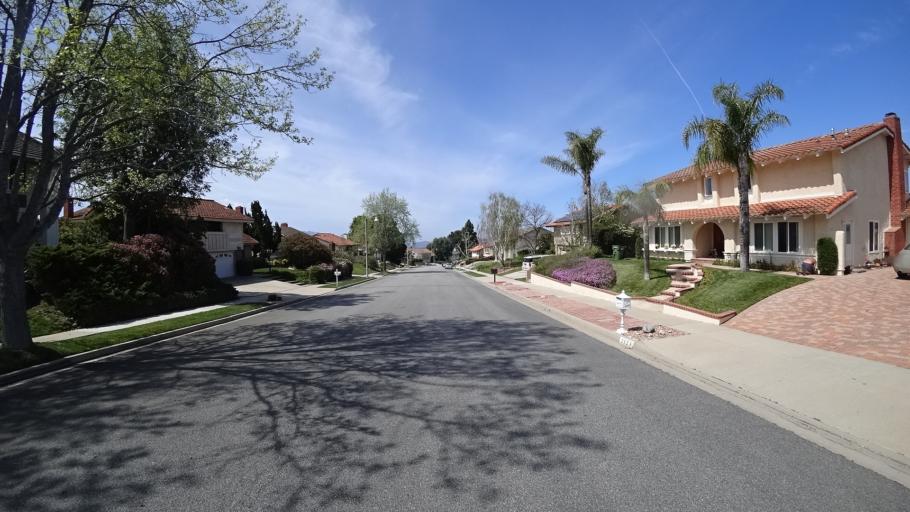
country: US
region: California
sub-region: Ventura County
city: Thousand Oaks
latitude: 34.2269
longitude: -118.8321
